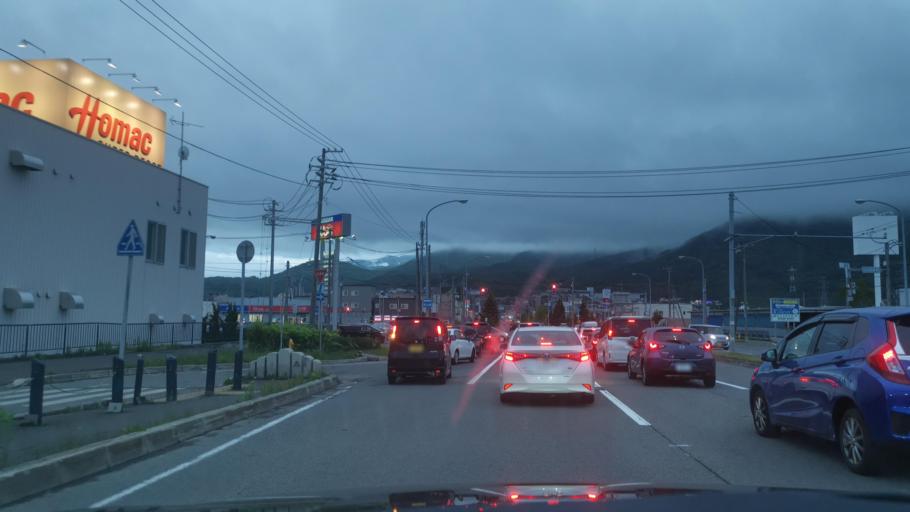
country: JP
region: Hokkaido
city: Sapporo
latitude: 43.1024
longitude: 141.2705
